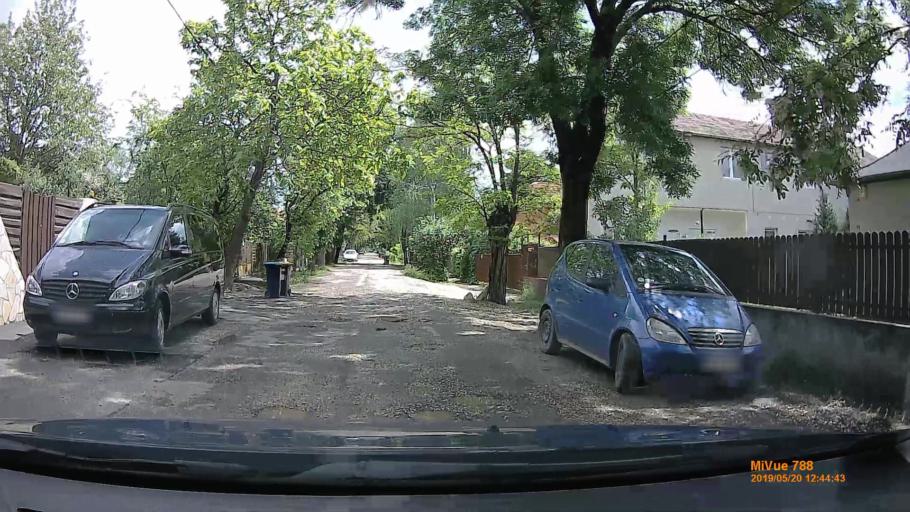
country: HU
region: Budapest
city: Budapest XVII. keruelet
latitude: 47.4660
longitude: 19.2382
